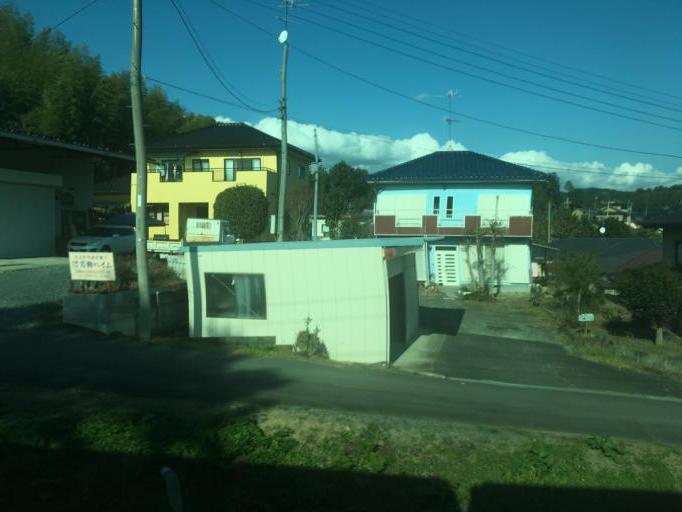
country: JP
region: Ibaraki
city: Kasama
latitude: 36.3652
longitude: 140.2589
